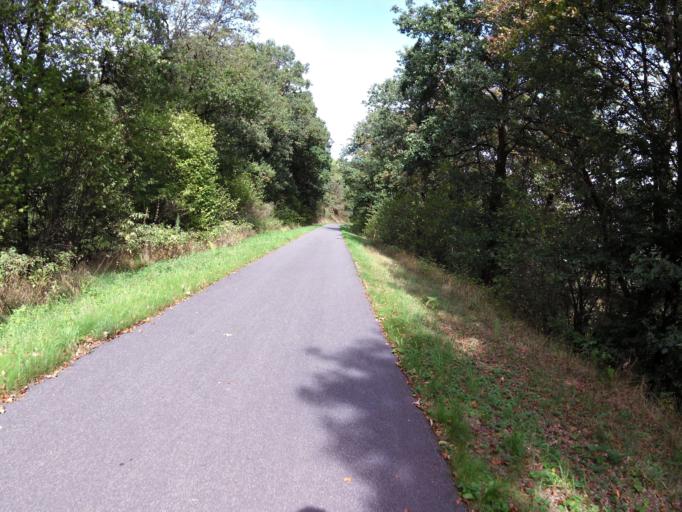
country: DE
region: Rheinland-Pfalz
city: Euscheid
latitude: 50.1268
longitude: 6.3021
